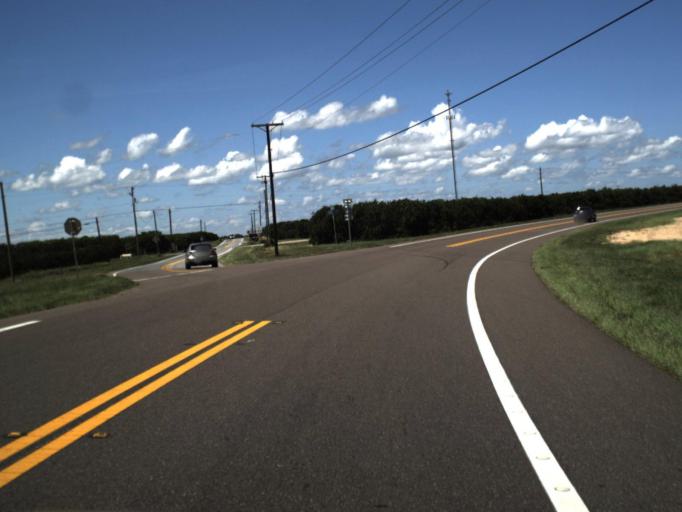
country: US
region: Florida
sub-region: Polk County
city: Crooked Lake Park
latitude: 27.8429
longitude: -81.5696
